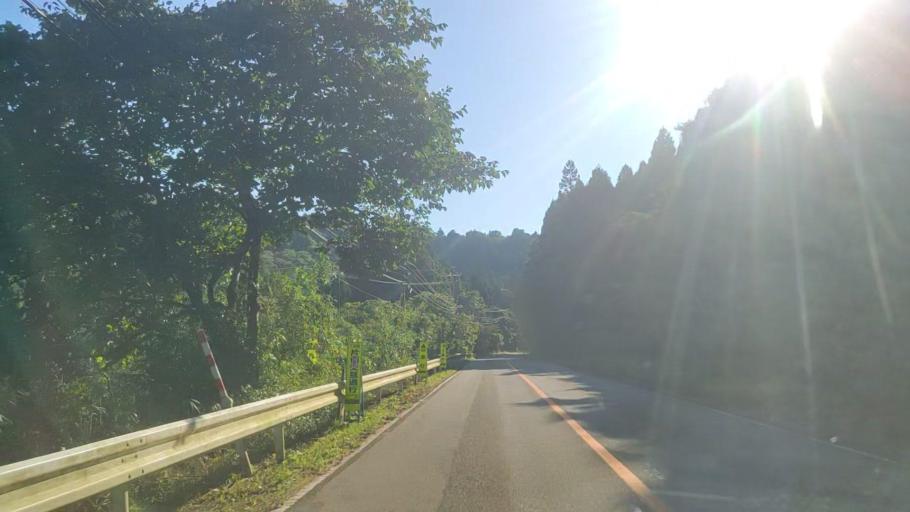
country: JP
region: Ishikawa
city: Nanao
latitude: 37.1402
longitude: 136.8680
